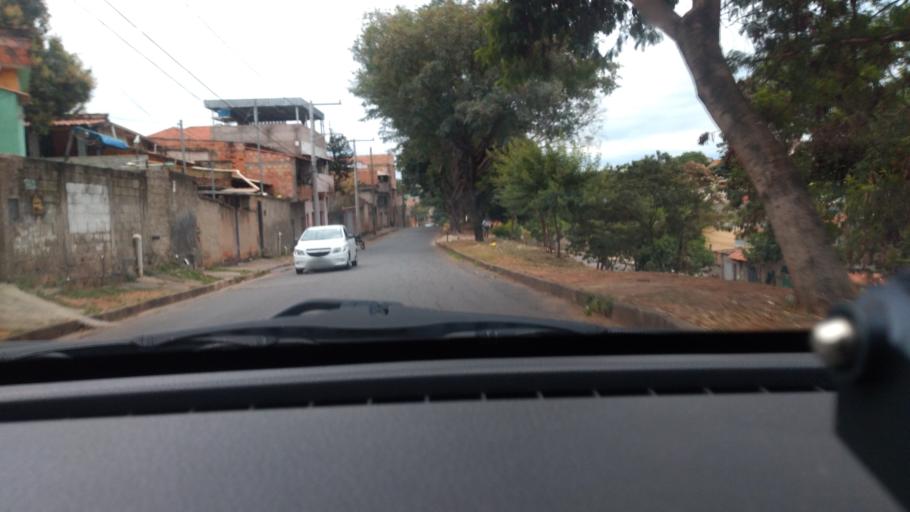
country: BR
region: Minas Gerais
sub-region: Belo Horizonte
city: Belo Horizonte
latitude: -19.8307
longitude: -43.9347
